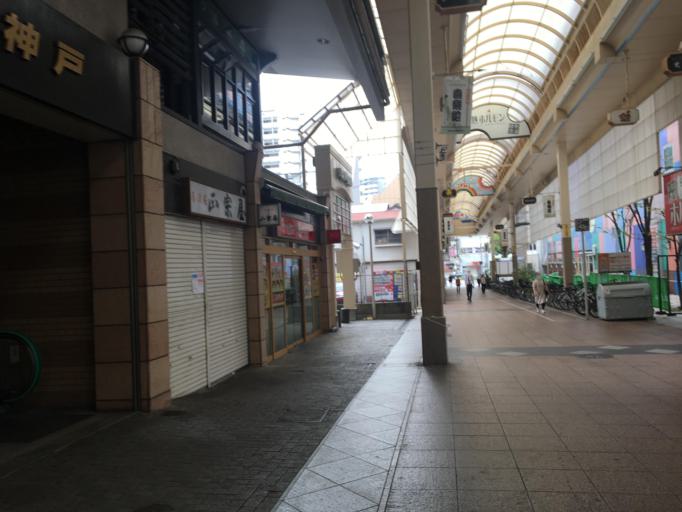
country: JP
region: Hyogo
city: Kobe
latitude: 34.6777
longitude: 135.1697
